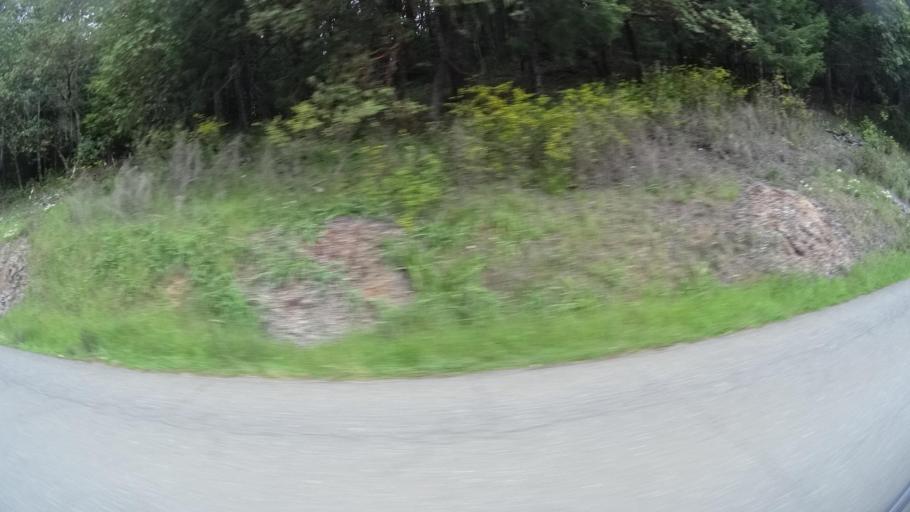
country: US
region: California
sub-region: Humboldt County
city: Redway
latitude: 40.2900
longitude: -123.8119
